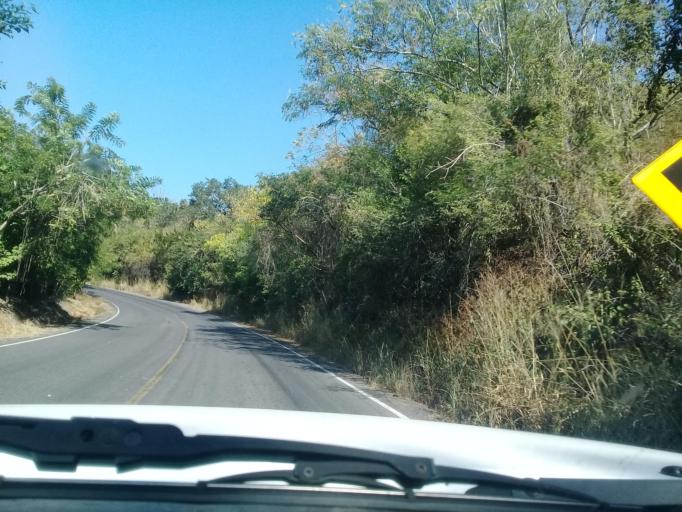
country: MX
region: Veracruz
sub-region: Emiliano Zapata
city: Plan del Rio
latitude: 19.4144
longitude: -96.6128
